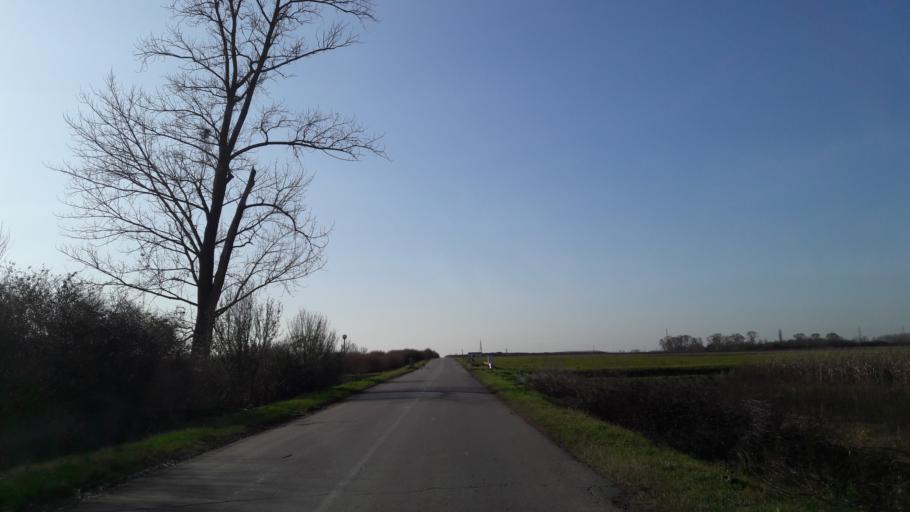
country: HR
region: Osjecko-Baranjska
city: Tenja
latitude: 45.4899
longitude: 18.7311
